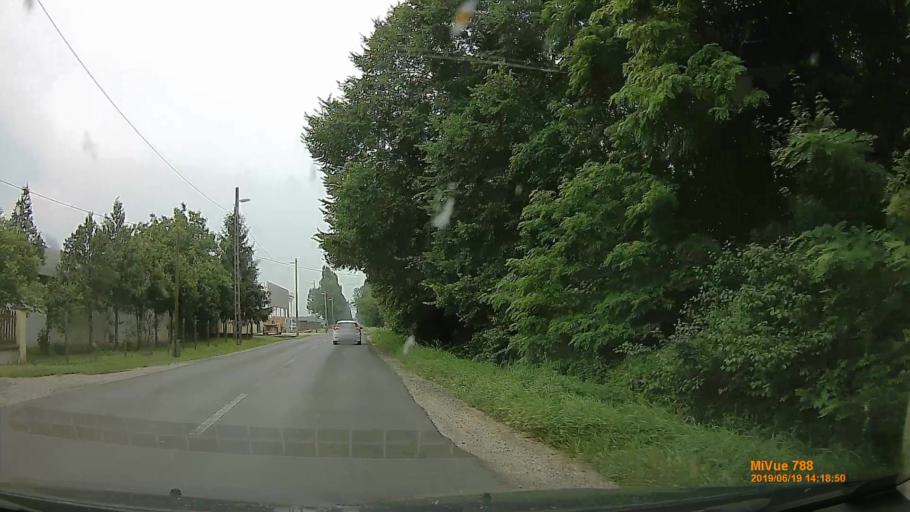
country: HU
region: Baranya
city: Szigetvar
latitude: 46.0386
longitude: 17.7822
